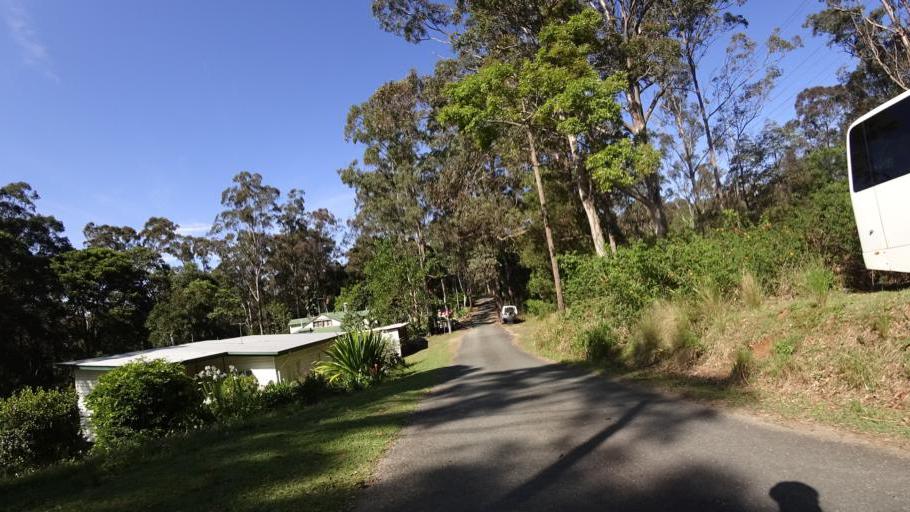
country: AU
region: Queensland
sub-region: Moreton Bay
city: Highvale
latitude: -27.3991
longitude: 152.7832
